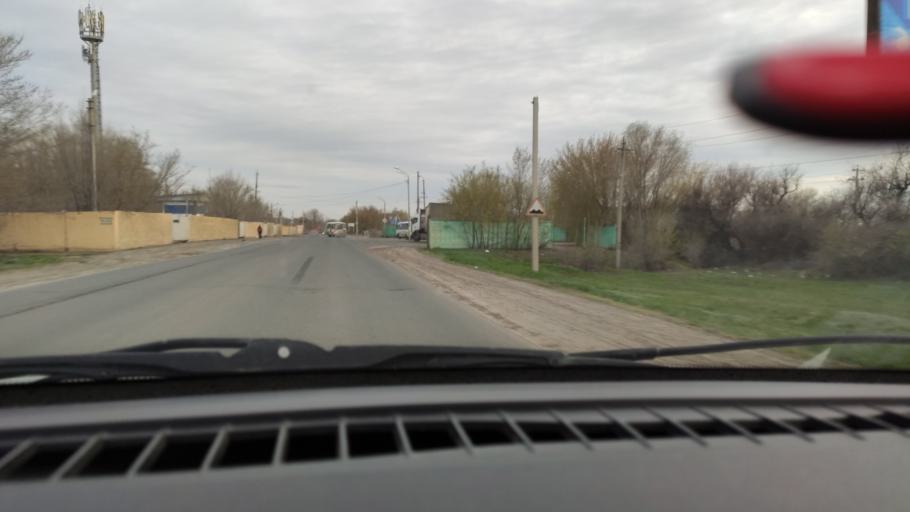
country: RU
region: Orenburg
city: Tatarskaya Kargala
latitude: 51.8832
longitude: 55.1527
